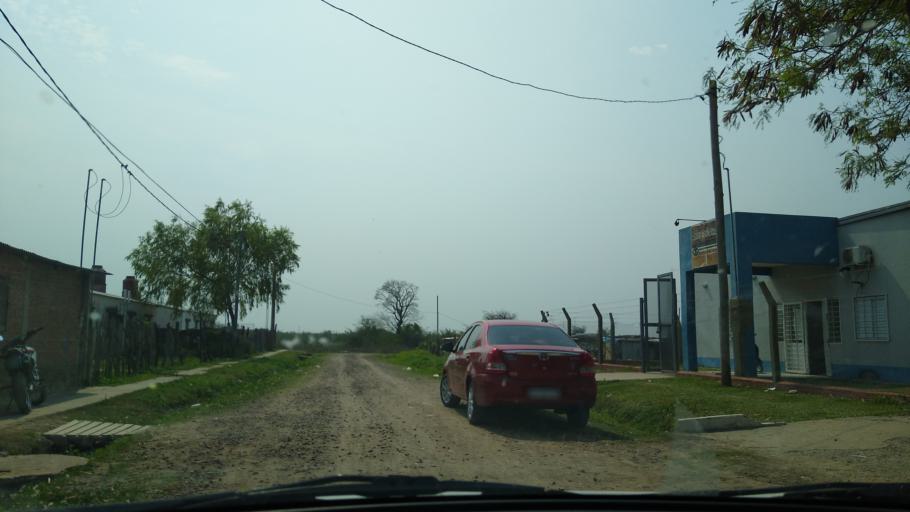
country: AR
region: Chaco
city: Fontana
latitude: -27.4003
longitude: -58.9854
